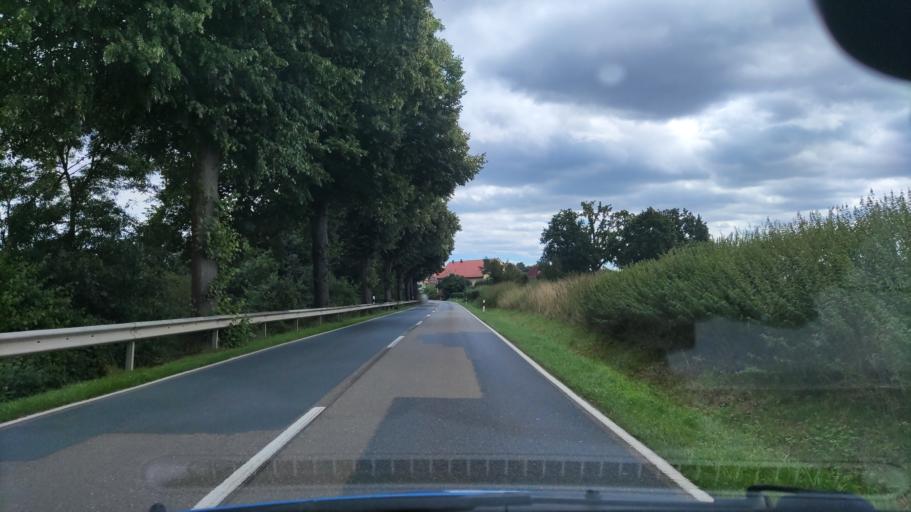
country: DE
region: Lower Saxony
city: Einbeck
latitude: 51.8277
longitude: 9.8099
